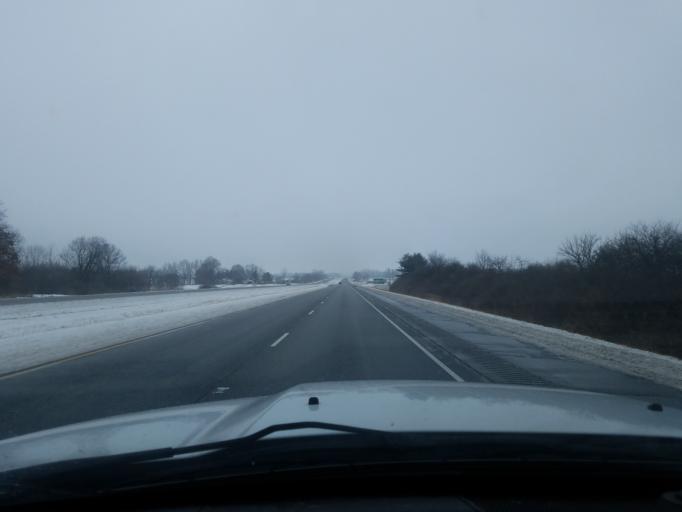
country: US
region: Indiana
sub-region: Fulton County
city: Rochester
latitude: 40.9425
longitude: -86.1683
